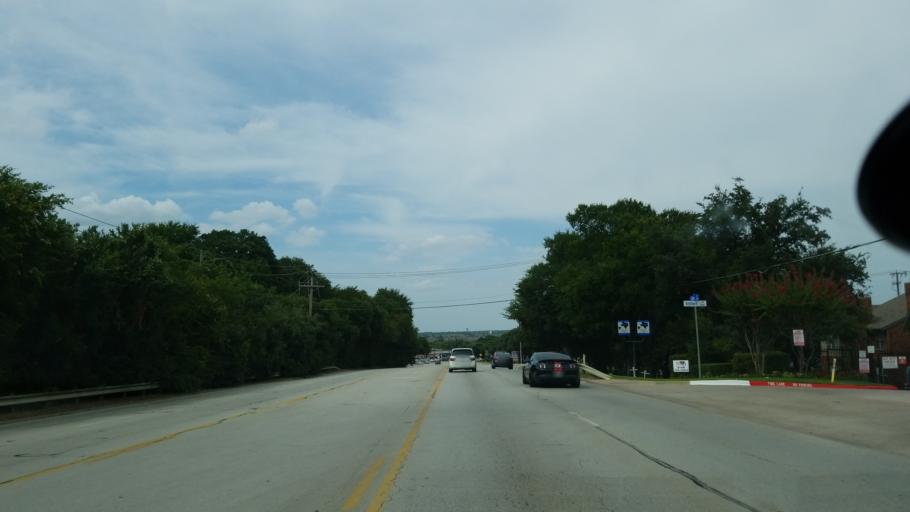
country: US
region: Texas
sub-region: Tarrant County
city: Arlington
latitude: 32.7812
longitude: -97.0961
